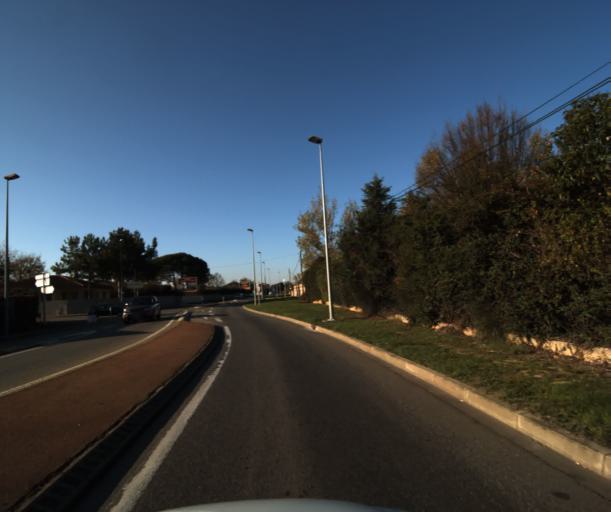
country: FR
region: Midi-Pyrenees
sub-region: Departement de la Haute-Garonne
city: Colomiers
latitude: 43.6209
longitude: 1.3357
